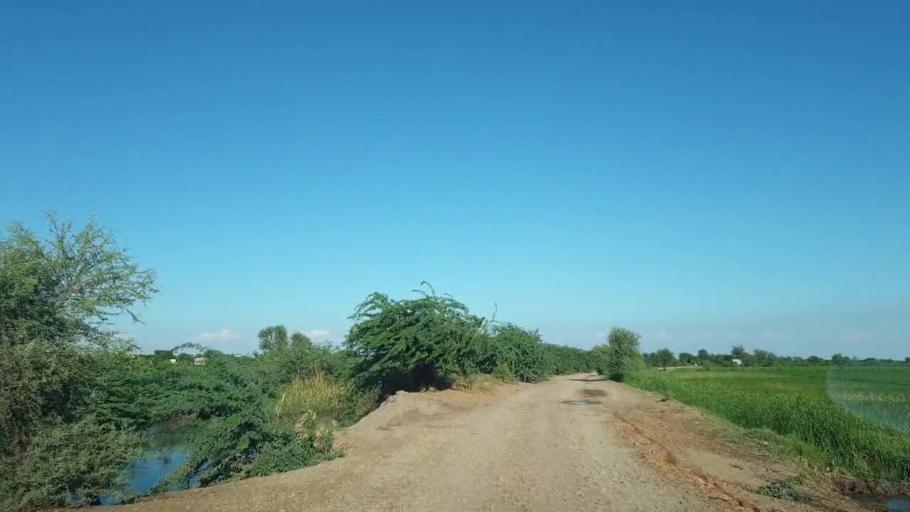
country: PK
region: Sindh
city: Dhoro Naro
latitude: 25.6382
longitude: 69.5061
